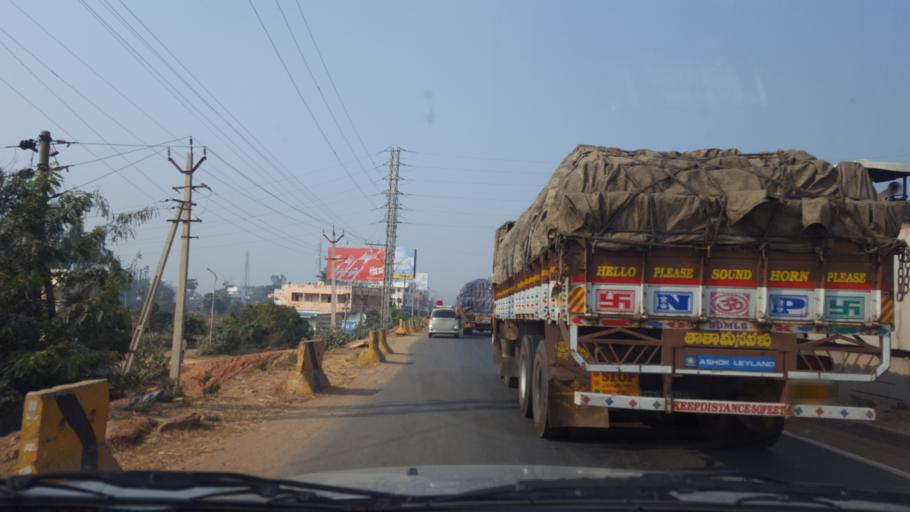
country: IN
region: Andhra Pradesh
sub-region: Srikakulam
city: Srikakulam
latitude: 18.2726
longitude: 83.8070
